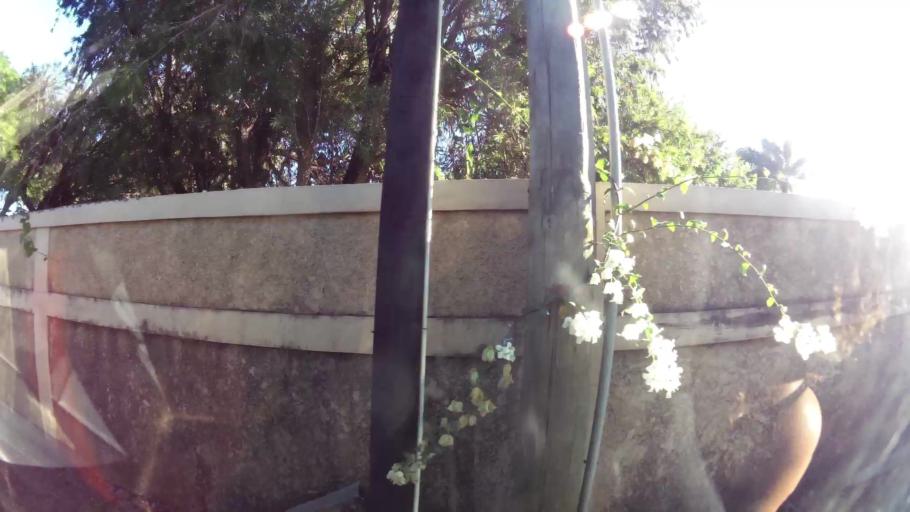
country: MU
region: Black River
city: Tamarin
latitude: -20.3361
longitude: 57.3752
